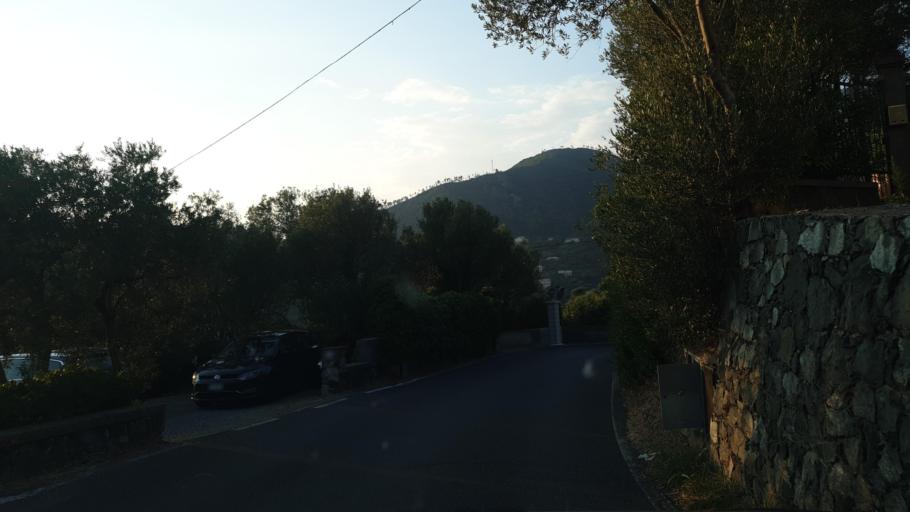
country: IT
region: Liguria
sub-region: Provincia di La Spezia
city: Bonassola
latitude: 44.1808
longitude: 9.5866
